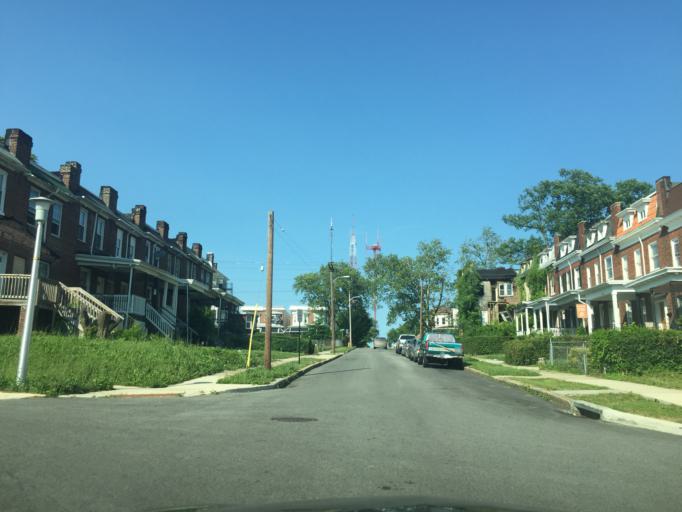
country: US
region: Maryland
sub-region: Baltimore County
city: Lochearn
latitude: 39.3296
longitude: -76.6624
